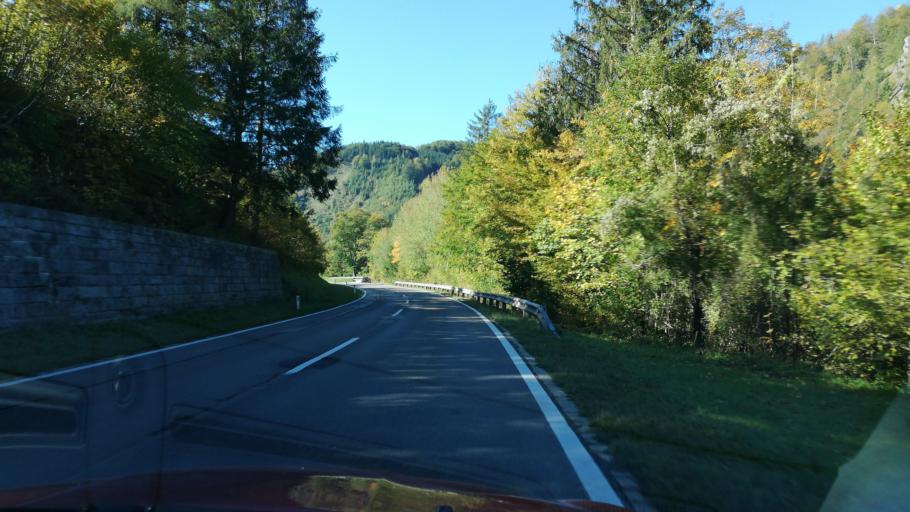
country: AT
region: Styria
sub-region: Politischer Bezirk Liezen
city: Altenmarkt bei Sankt Gallen
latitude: 47.7689
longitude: 14.6511
